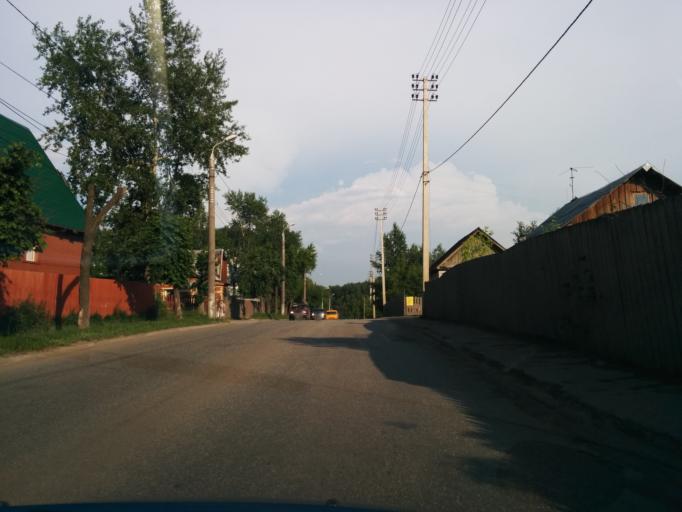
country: RU
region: Perm
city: Perm
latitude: 58.1164
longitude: 56.2944
